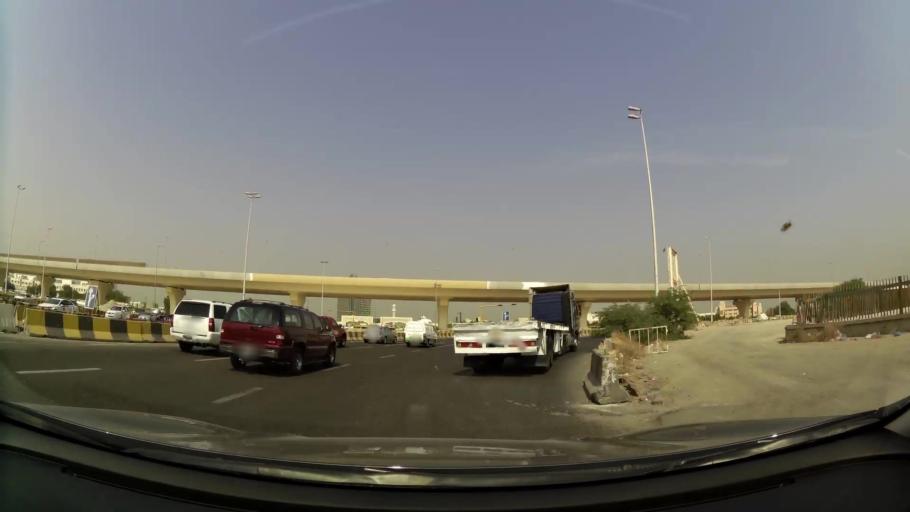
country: KW
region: Al Asimah
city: Ar Rabiyah
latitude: 29.3260
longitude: 47.9211
